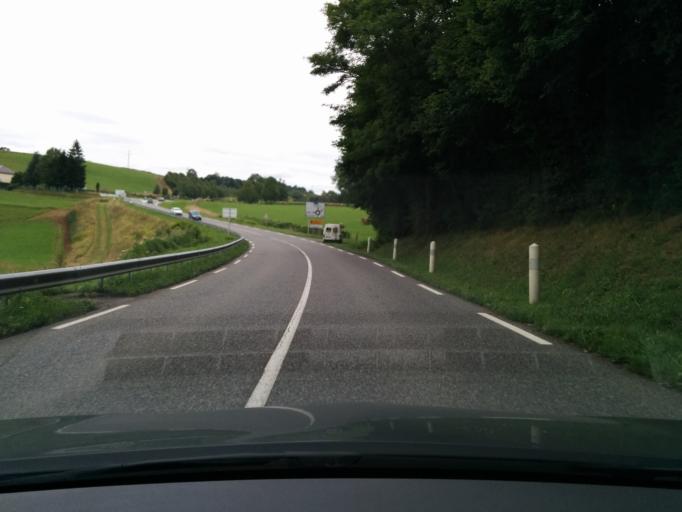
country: FR
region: Midi-Pyrenees
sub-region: Departement des Hautes-Pyrenees
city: La Barthe-de-Neste
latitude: 43.0254
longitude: 0.3716
